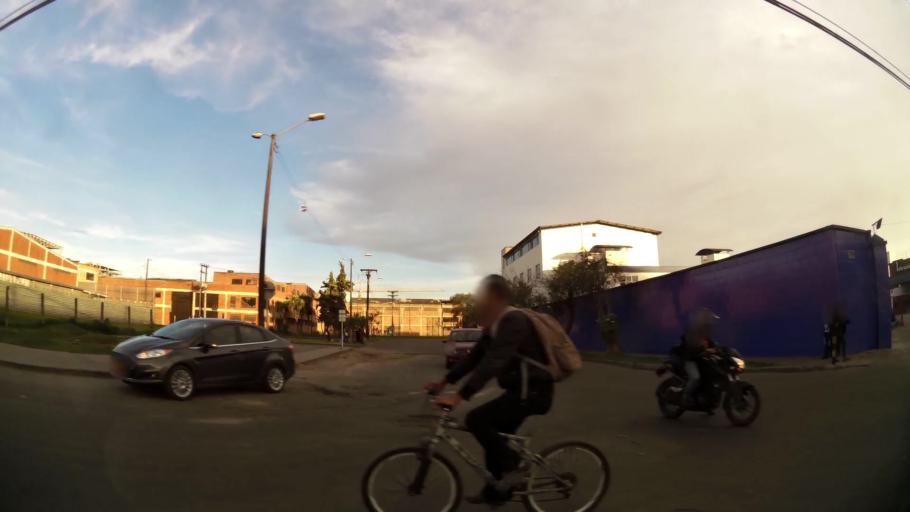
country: CO
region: Cundinamarca
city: Funza
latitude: 4.6913
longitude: -74.1623
